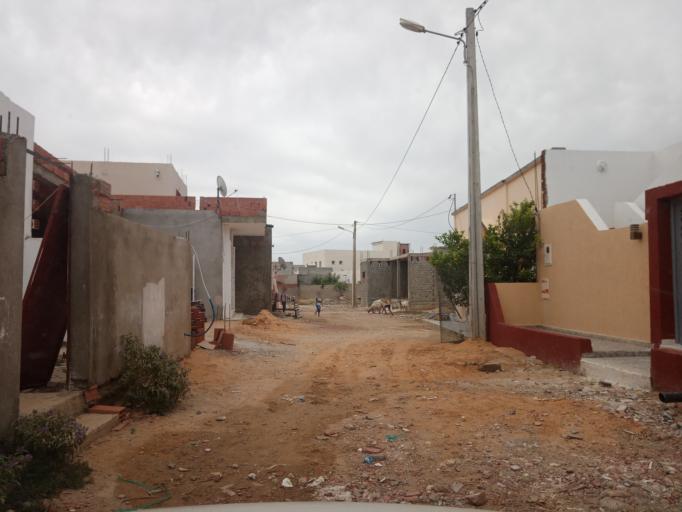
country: TN
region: Al Qayrawan
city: Sbikha
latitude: 36.1145
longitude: 10.0921
